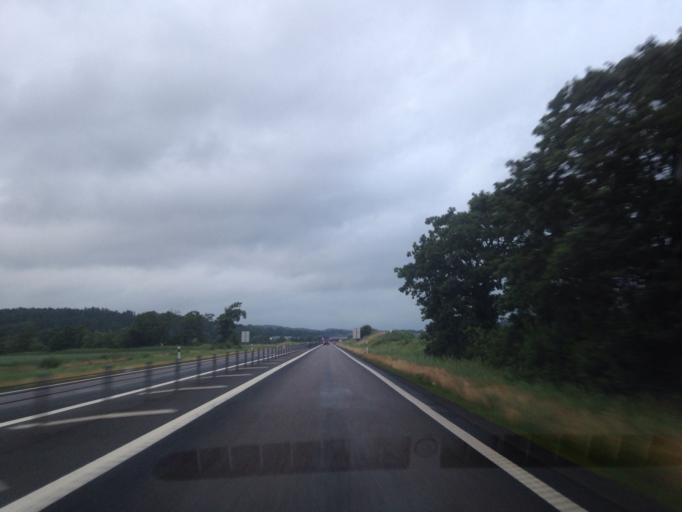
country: SE
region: Halland
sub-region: Varbergs Kommun
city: Varberg
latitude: 57.1560
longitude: 12.2708
